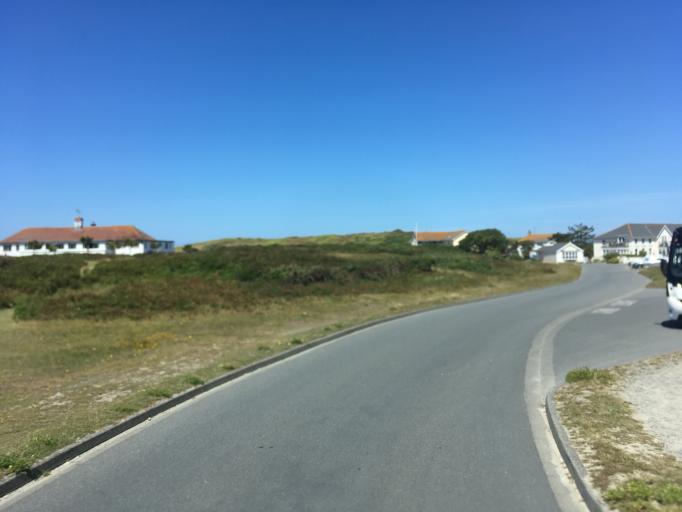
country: GG
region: St Peter Port
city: Saint Peter Port
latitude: 49.5042
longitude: -2.5341
